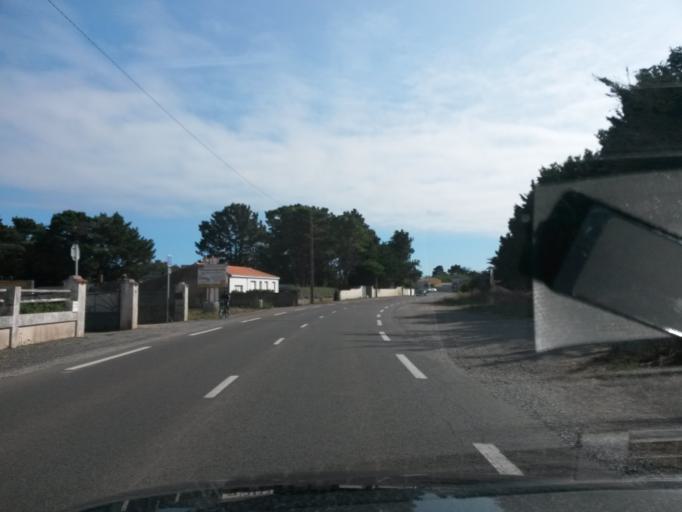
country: FR
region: Pays de la Loire
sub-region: Departement de la Vendee
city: Olonne-sur-Mer
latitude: 46.5516
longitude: -1.8065
